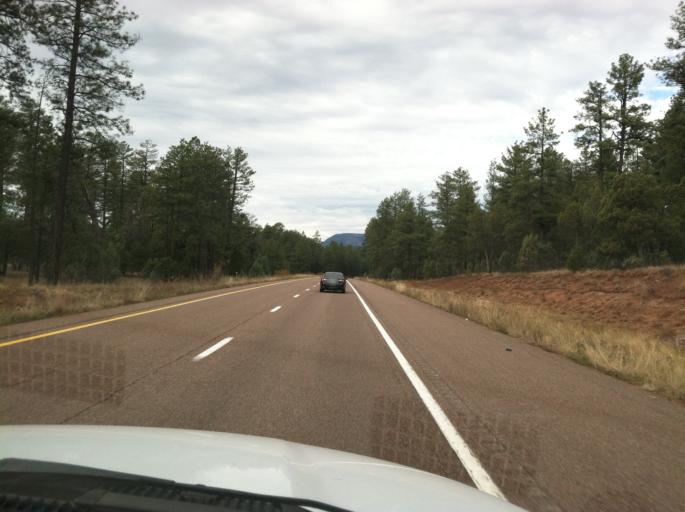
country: US
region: Arizona
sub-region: Gila County
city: Star Valley
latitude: 34.2950
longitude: -110.9794
